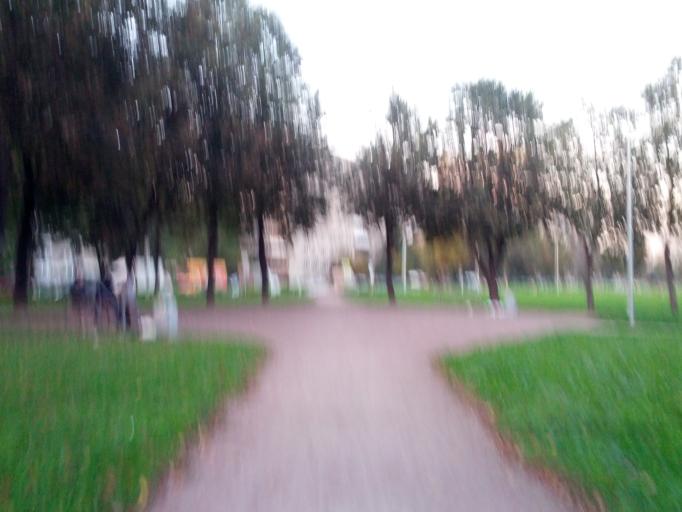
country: RU
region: St.-Petersburg
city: Obukhovo
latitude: 59.8967
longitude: 30.4691
